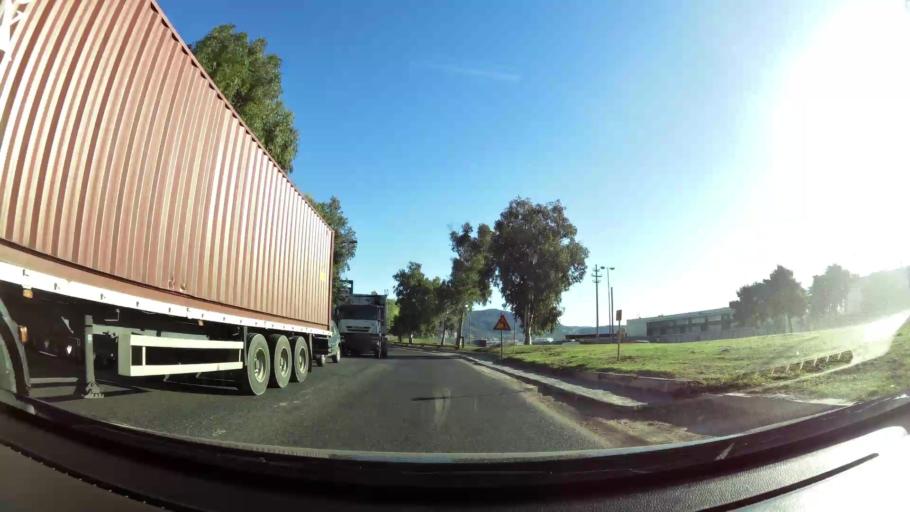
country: GR
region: Attica
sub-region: Nomarchia Athinas
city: Skaramangas
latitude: 38.0301
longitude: 23.5976
